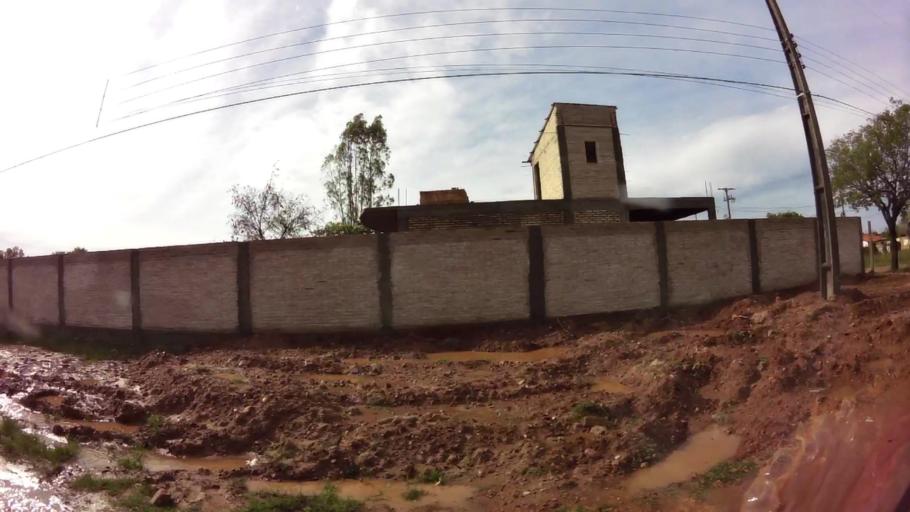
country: PY
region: Central
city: Limpio
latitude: -25.1749
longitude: -57.4949
